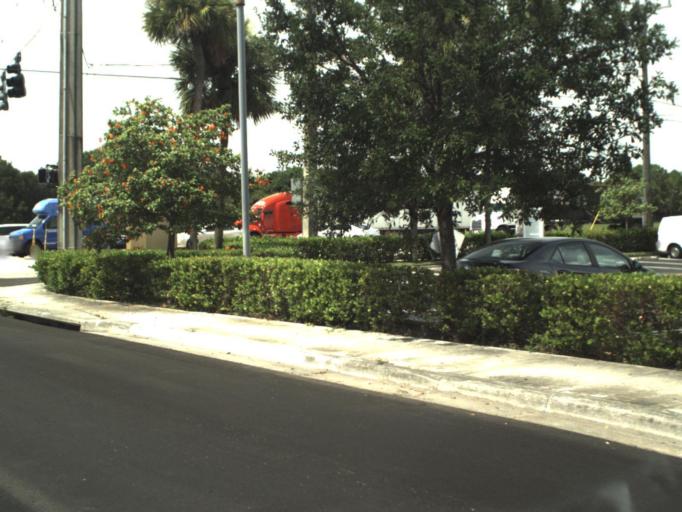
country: US
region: Florida
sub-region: Palm Beach County
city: West Palm Beach
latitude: 26.6913
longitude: -80.0751
